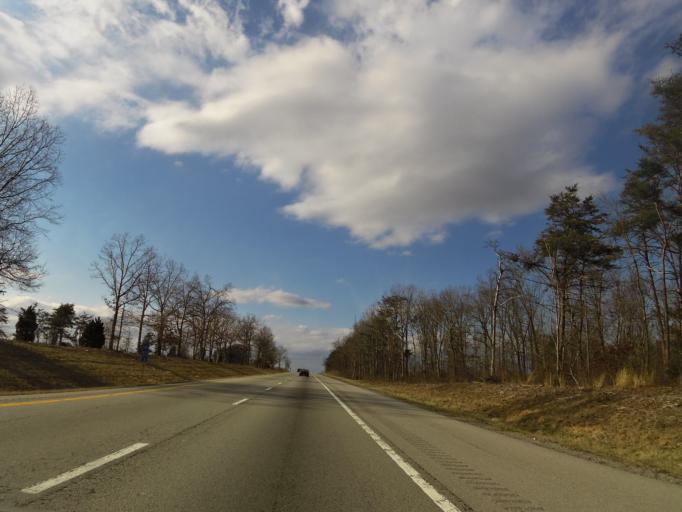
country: US
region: Tennessee
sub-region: Cumberland County
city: Fairfield Glade
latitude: 35.9367
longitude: -84.9249
